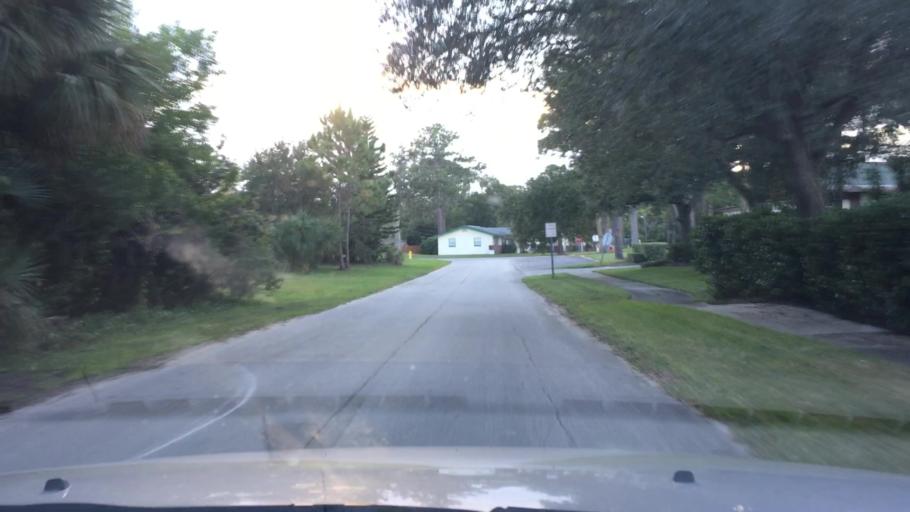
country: US
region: Florida
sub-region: Volusia County
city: Port Orange
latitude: 29.1335
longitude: -80.9843
